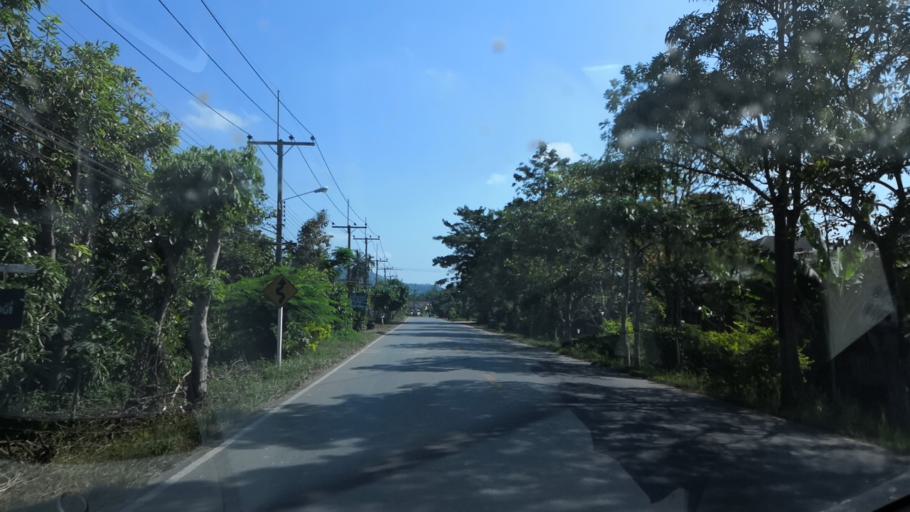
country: TH
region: Chiang Rai
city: Wiang Chai
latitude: 19.8789
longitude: 99.9432
